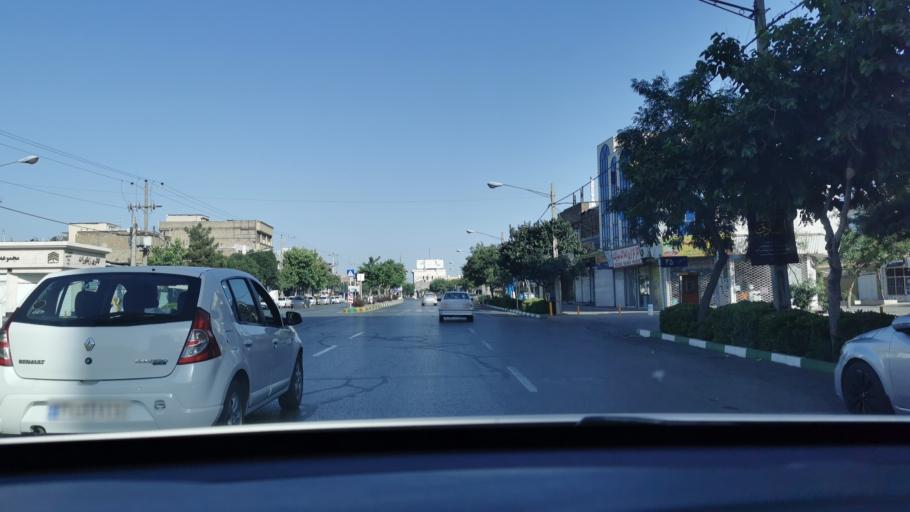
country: IR
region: Razavi Khorasan
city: Mashhad
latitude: 36.3331
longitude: 59.5140
